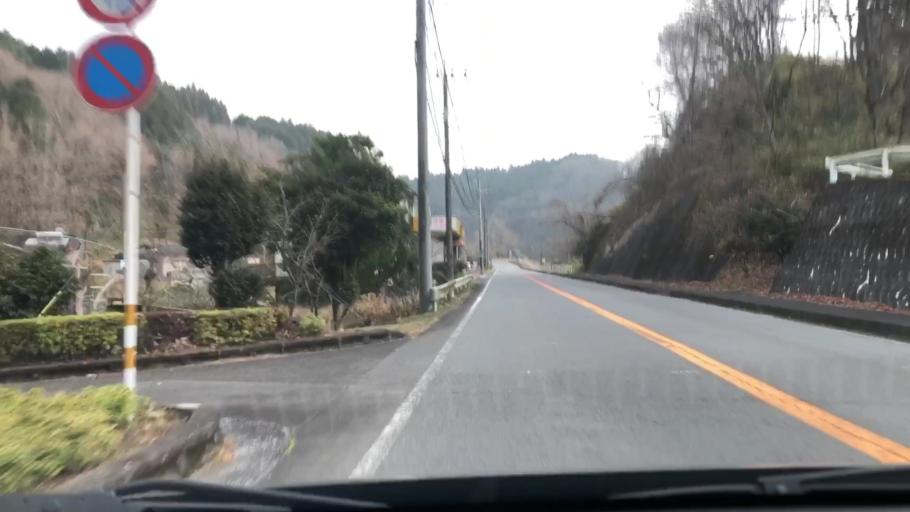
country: JP
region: Oita
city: Takedamachi
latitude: 32.9734
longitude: 131.5257
